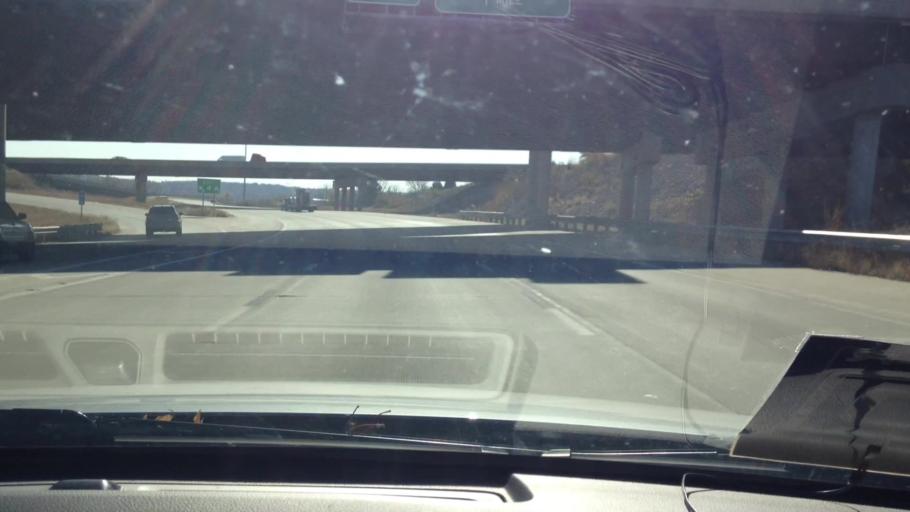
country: US
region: Kansas
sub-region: Wyandotte County
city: Kansas City
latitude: 39.1060
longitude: -94.6806
